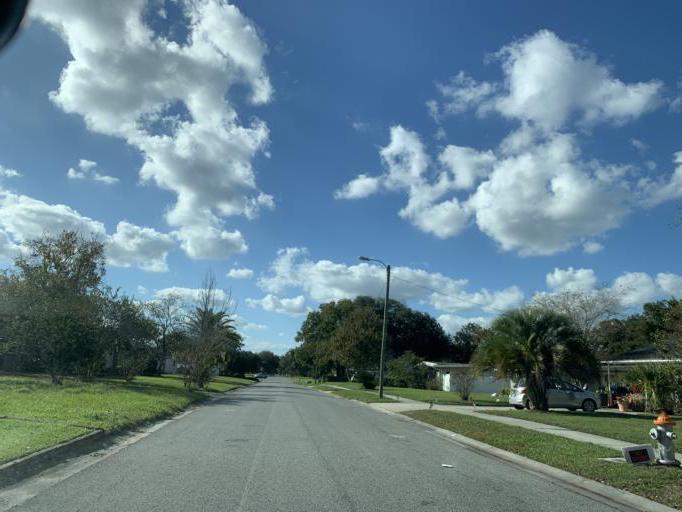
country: US
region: Florida
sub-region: Orange County
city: Eatonville
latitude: 28.6106
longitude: -81.3973
